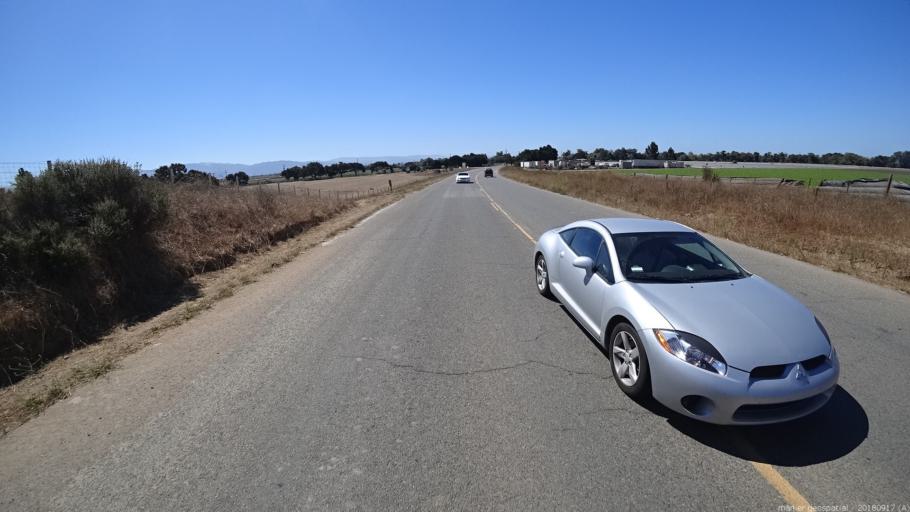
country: US
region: California
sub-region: Monterey County
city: Salinas
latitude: 36.7347
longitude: -121.6060
